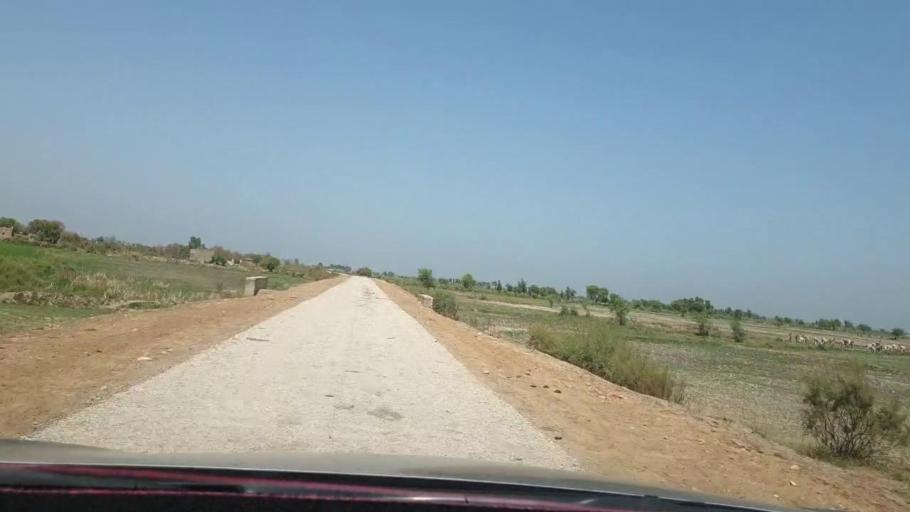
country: PK
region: Sindh
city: Warah
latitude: 27.5156
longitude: 67.7071
